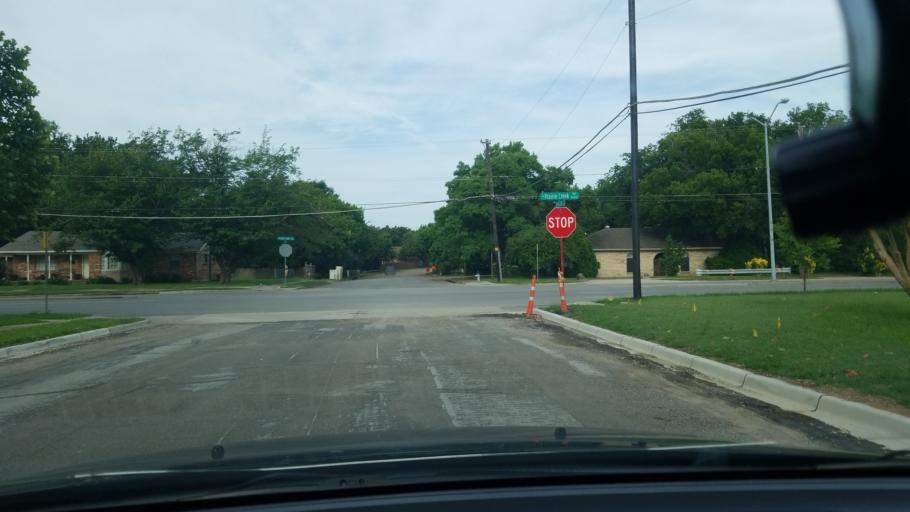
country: US
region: Texas
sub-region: Dallas County
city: Balch Springs
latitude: 32.7550
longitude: -96.6649
